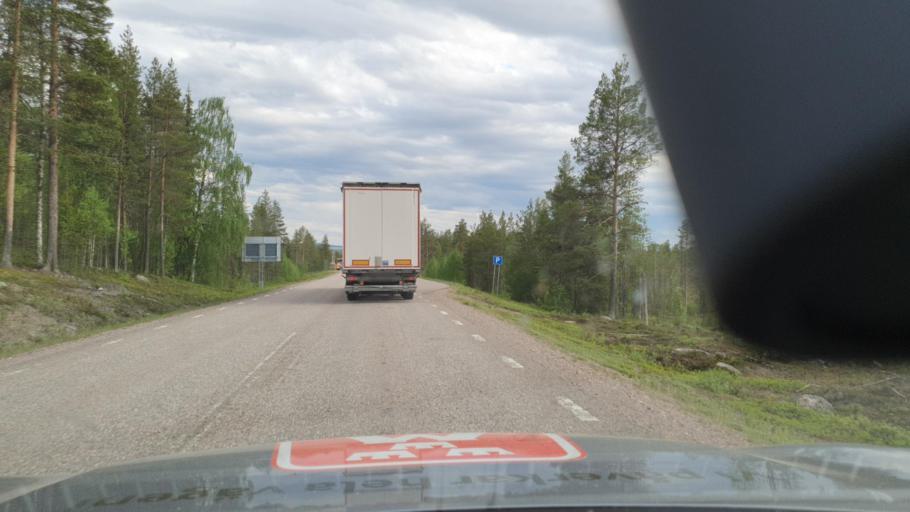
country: SE
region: Norrbotten
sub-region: Gallivare Kommun
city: Gaellivare
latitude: 67.1355
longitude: 20.9035
